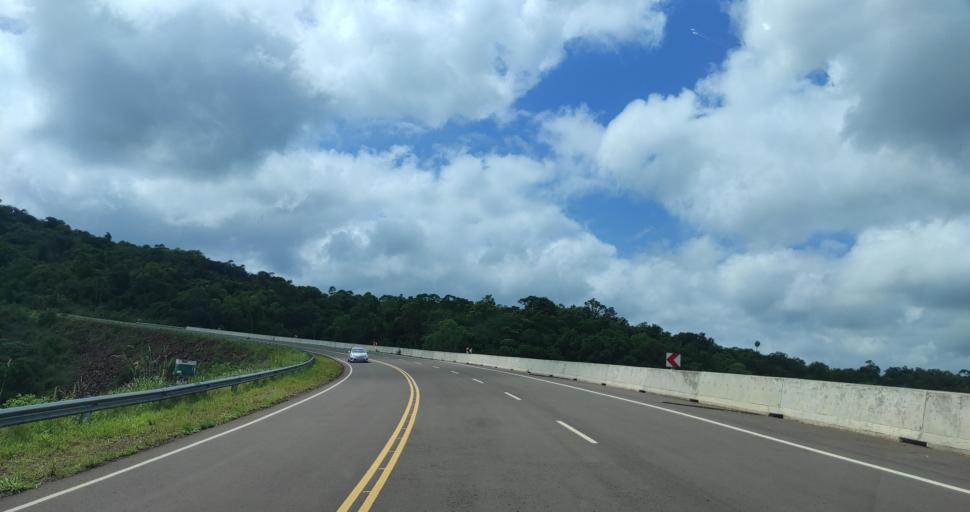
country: AR
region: Misiones
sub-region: Departamento de Veinticinco de Mayo
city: Veinticinco de Mayo
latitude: -27.3830
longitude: -54.8181
